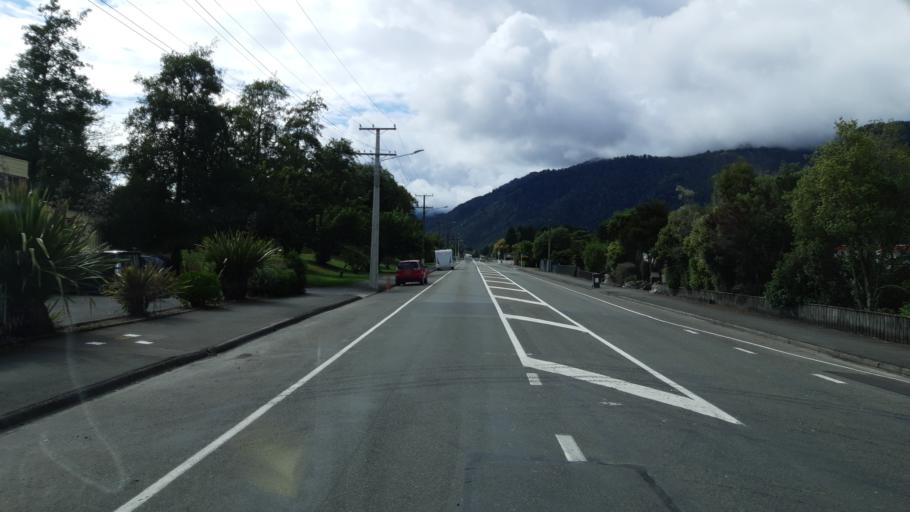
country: NZ
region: West Coast
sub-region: Buller District
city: Westport
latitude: -41.8001
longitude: 172.3274
